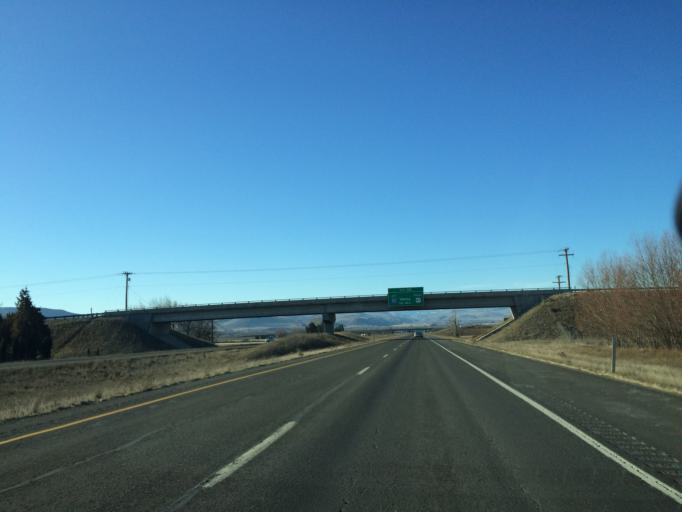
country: US
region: Washington
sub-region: Kittitas County
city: Ellensburg
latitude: 46.9708
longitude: -120.4961
